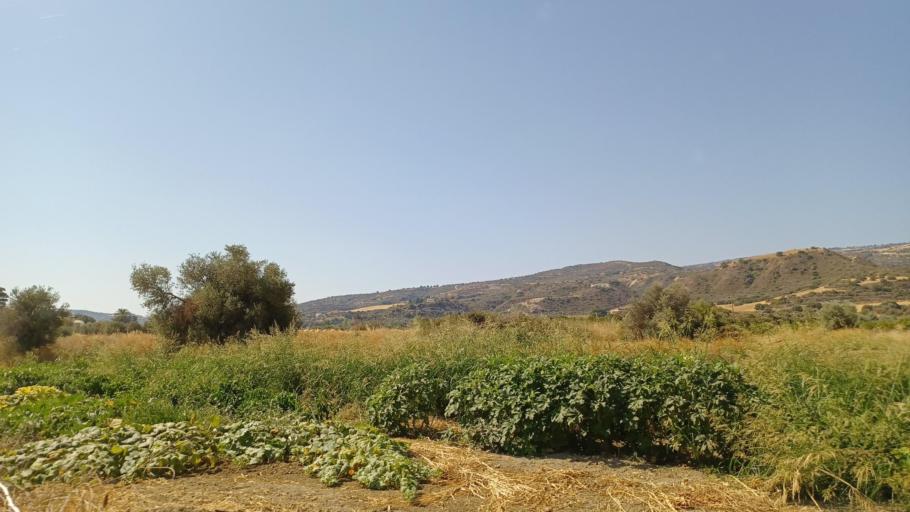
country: CY
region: Pafos
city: Polis
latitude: 35.0083
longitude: 32.4345
